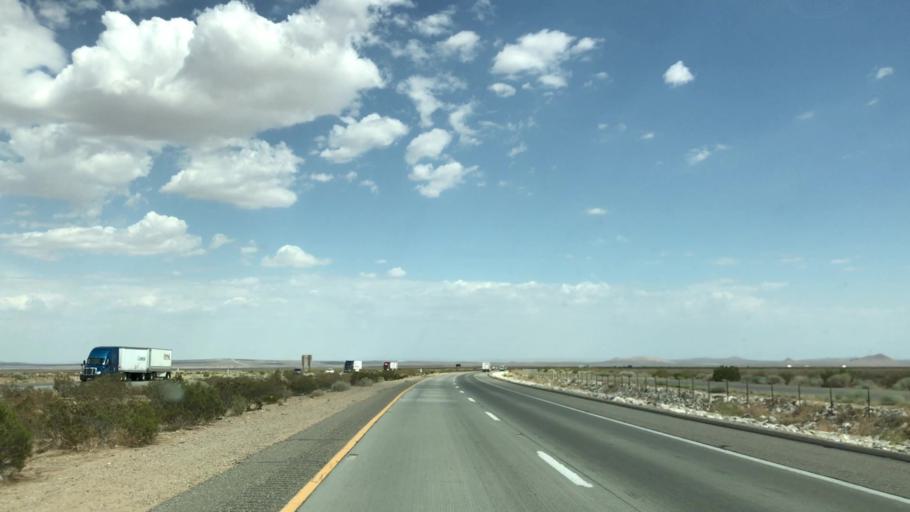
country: US
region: California
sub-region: Kern County
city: Mojave
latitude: 35.0893
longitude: -118.1251
